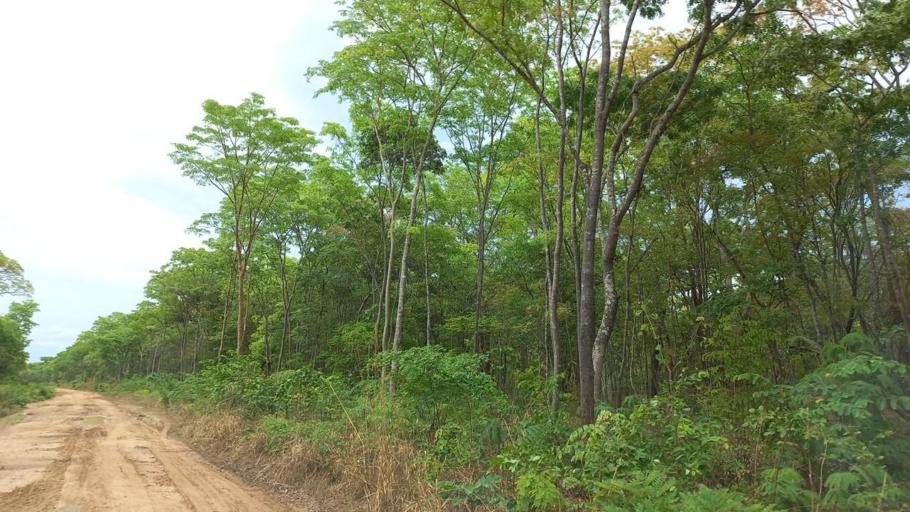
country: ZM
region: North-Western
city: Kalengwa
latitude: -13.5644
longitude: 24.9716
